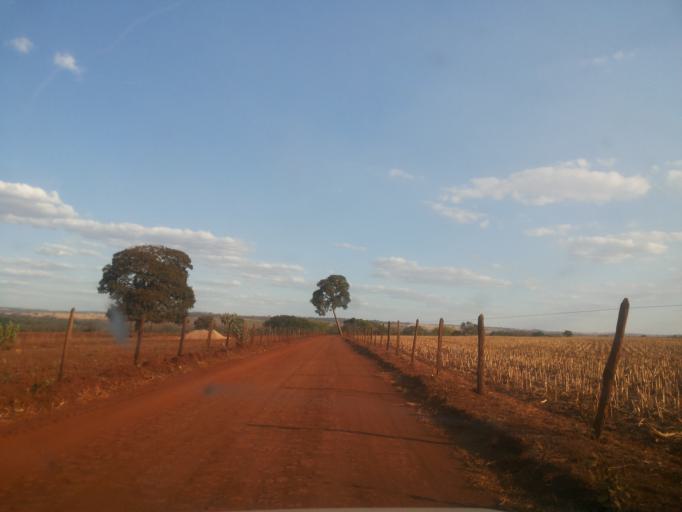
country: BR
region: Minas Gerais
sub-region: Capinopolis
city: Capinopolis
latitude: -18.6865
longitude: -49.3766
